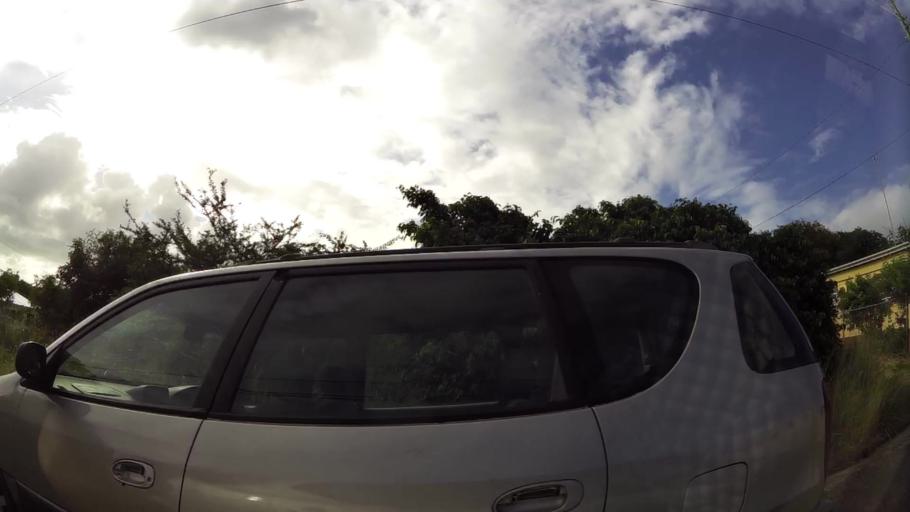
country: AG
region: Saint John
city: Saint John's
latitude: 17.1298
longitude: -61.8275
